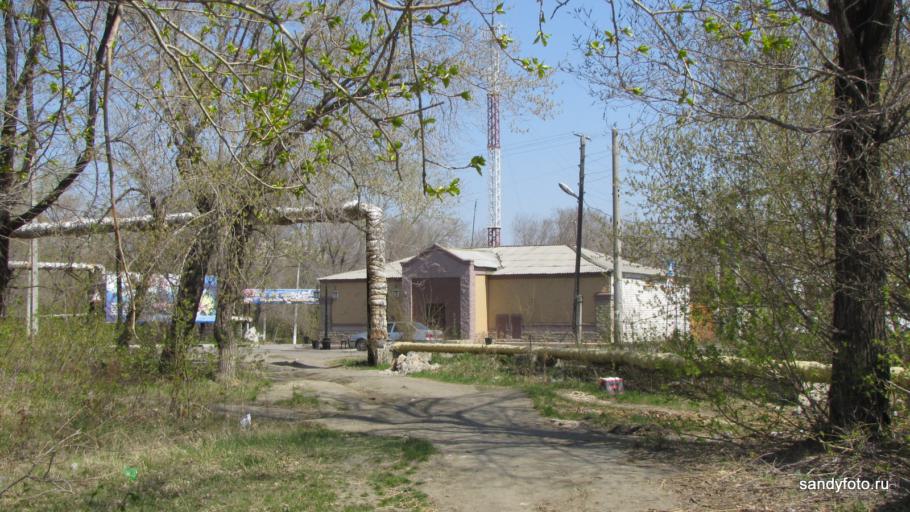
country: RU
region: Chelyabinsk
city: Troitsk
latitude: 54.1010
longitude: 61.5541
